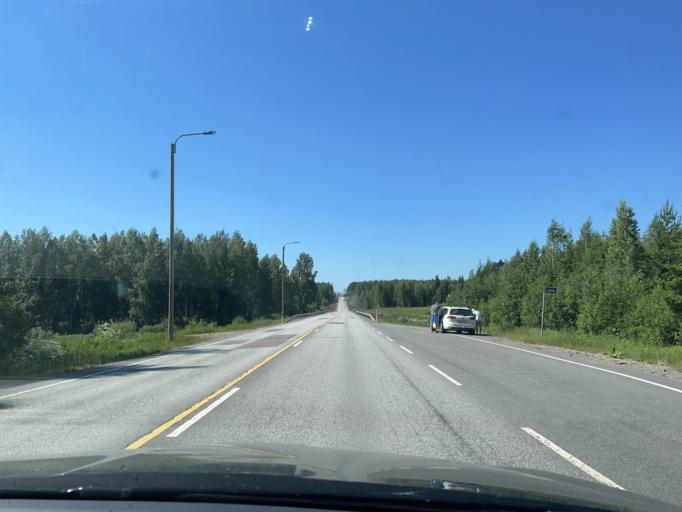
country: FI
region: Central Finland
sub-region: Saarijaervi-Viitasaari
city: Viitasaari
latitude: 63.1444
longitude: 25.8011
